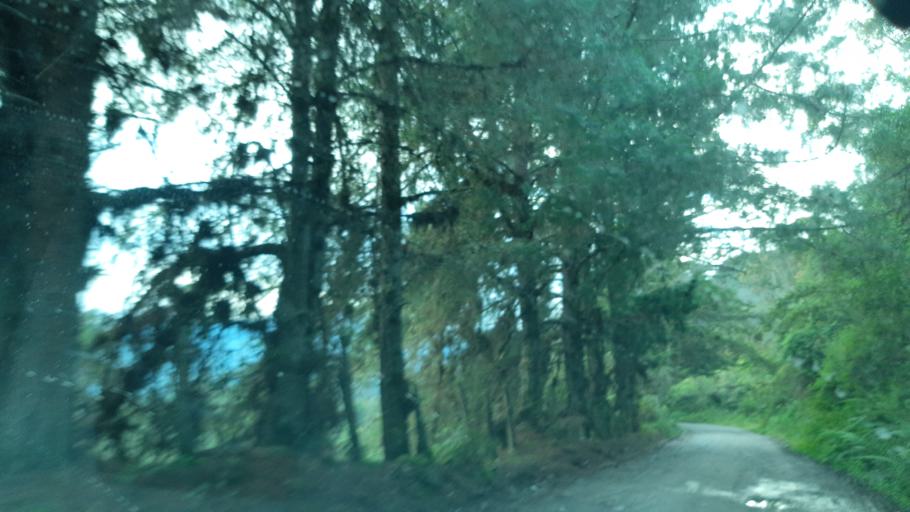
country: CO
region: Boyaca
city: Garagoa
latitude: 5.0833
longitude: -73.3190
